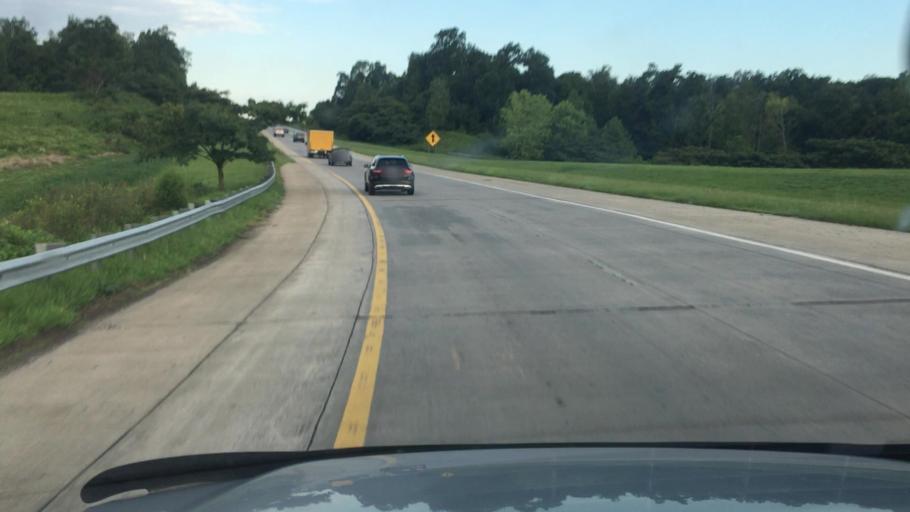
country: US
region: North Carolina
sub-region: Gaston County
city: Mount Holly
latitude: 35.2518
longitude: -80.9694
